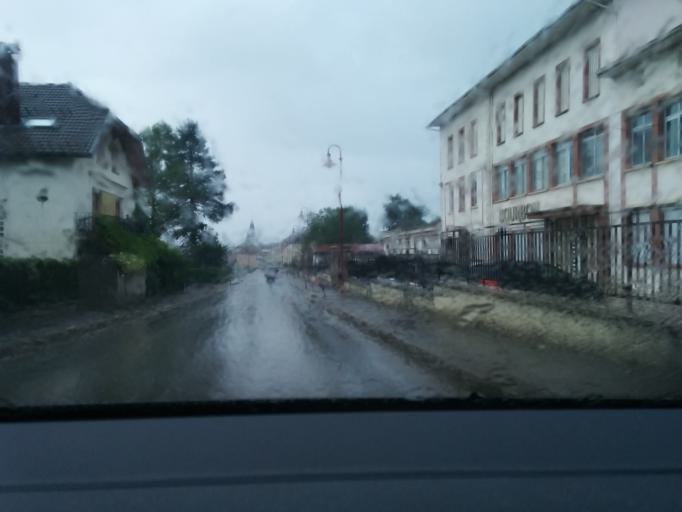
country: FR
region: Franche-Comte
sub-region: Departement du Jura
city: Saint-Lupicin
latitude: 46.4046
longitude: 5.7938
